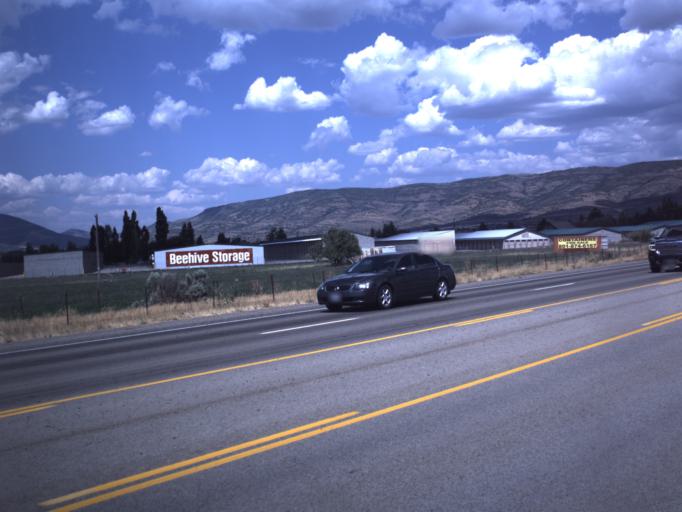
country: US
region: Utah
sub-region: Wasatch County
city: Heber
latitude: 40.4874
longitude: -111.4220
